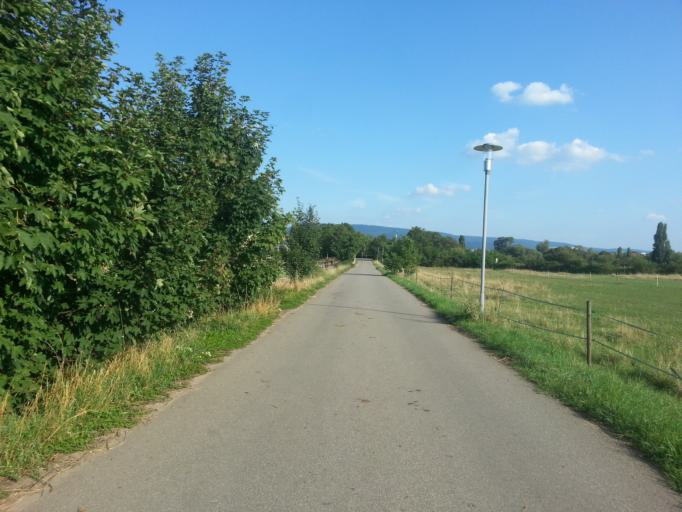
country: DE
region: Baden-Wuerttemberg
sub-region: Karlsruhe Region
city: Edingen-Neckarhausen
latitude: 49.4450
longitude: 8.6300
